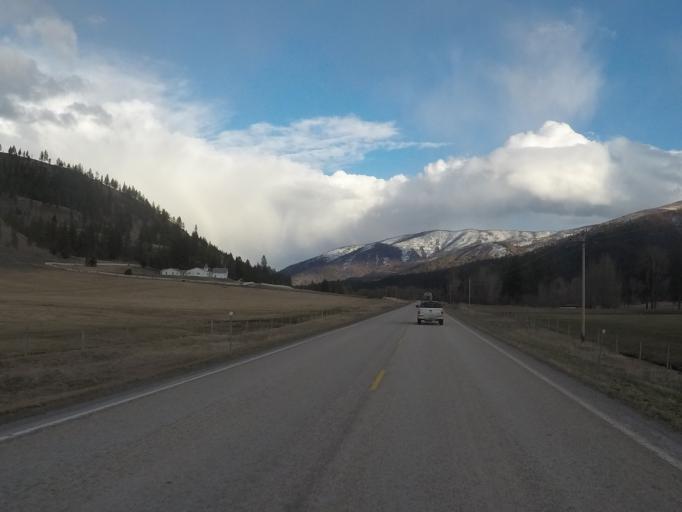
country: US
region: Montana
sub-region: Missoula County
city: Lolo
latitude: 46.7603
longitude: -114.2578
